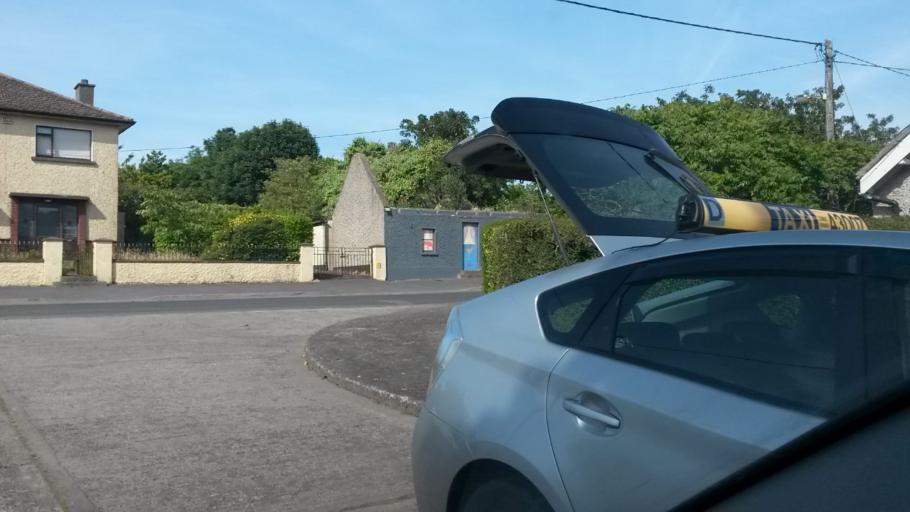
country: IE
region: Leinster
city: Lusk
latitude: 53.5262
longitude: -6.1689
